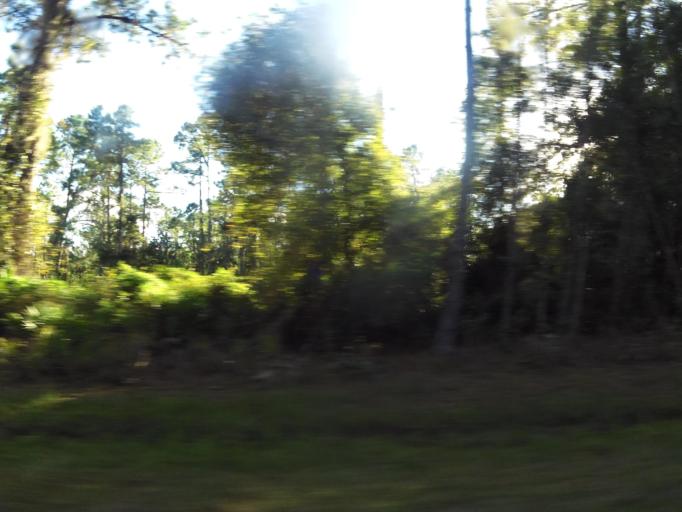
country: US
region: Florida
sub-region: Marion County
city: Citra
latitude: 29.4619
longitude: -82.1416
